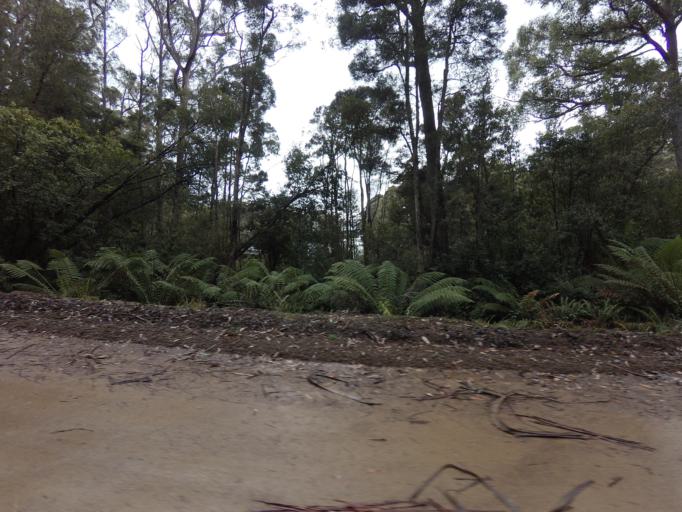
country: AU
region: Tasmania
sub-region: Huon Valley
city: Geeveston
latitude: -43.5550
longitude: 146.8839
